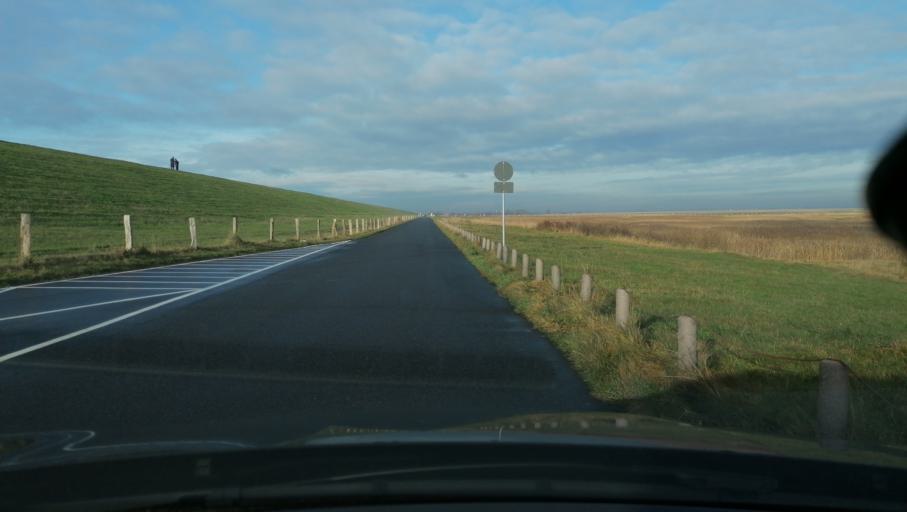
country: DE
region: Schleswig-Holstein
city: Friedrichsgabekoog
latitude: 54.0973
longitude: 8.9483
